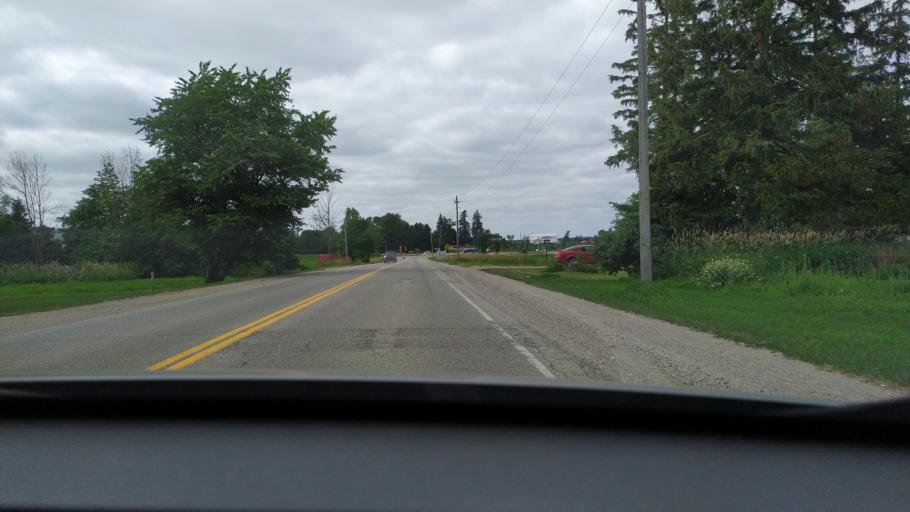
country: CA
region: Ontario
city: Stratford
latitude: 43.3138
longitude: -80.9832
